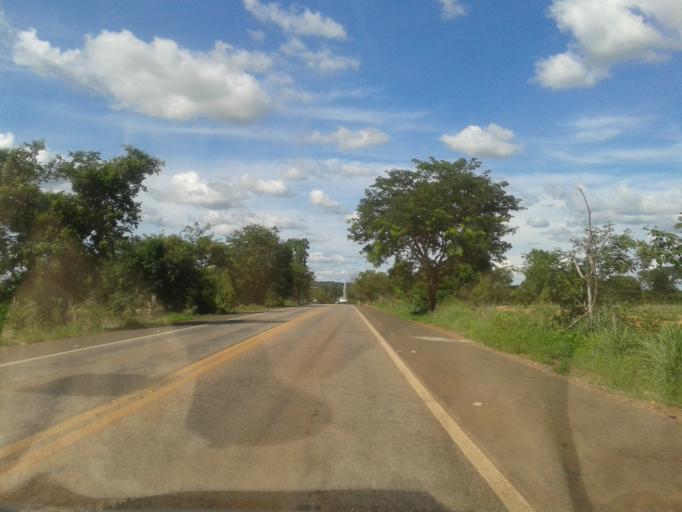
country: BR
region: Goias
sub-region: Mozarlandia
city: Mozarlandia
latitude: -15.0801
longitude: -50.6223
